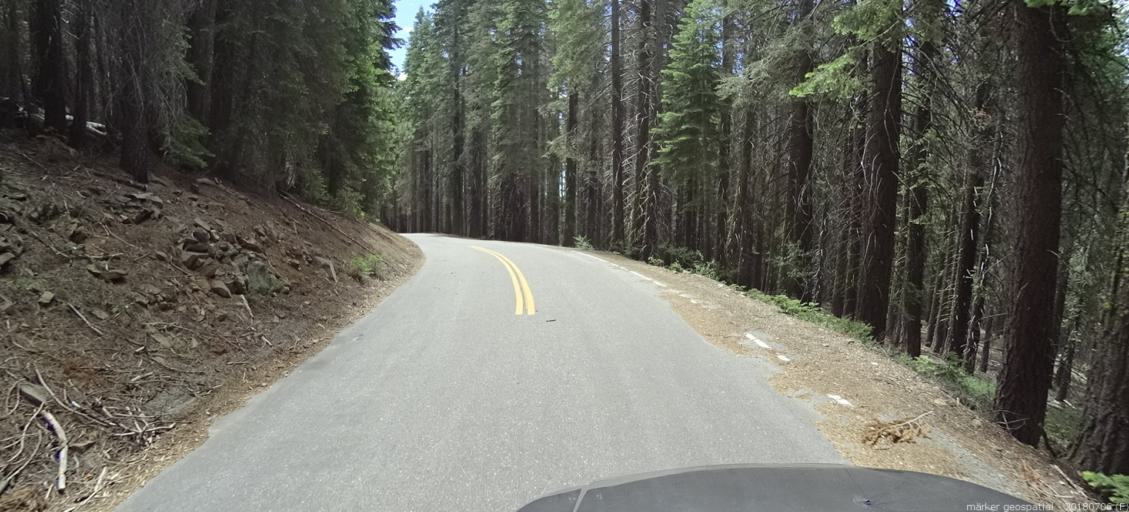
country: US
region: California
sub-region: Madera County
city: Oakhurst
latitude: 37.4258
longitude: -119.4277
